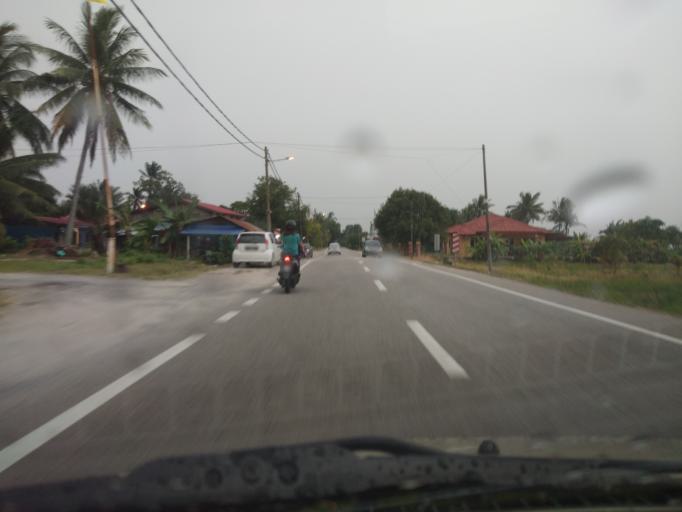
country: MY
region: Penang
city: Permatang Kuching
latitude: 5.4873
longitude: 100.4003
